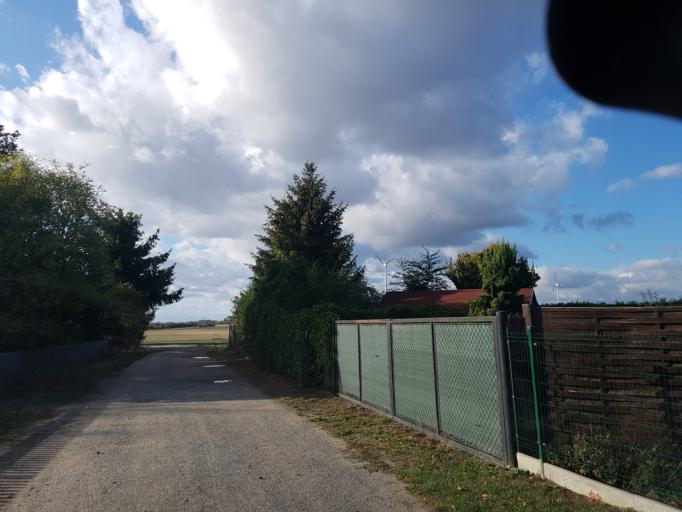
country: DE
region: Brandenburg
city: Doberlug-Kirchhain
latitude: 51.6117
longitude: 13.5970
